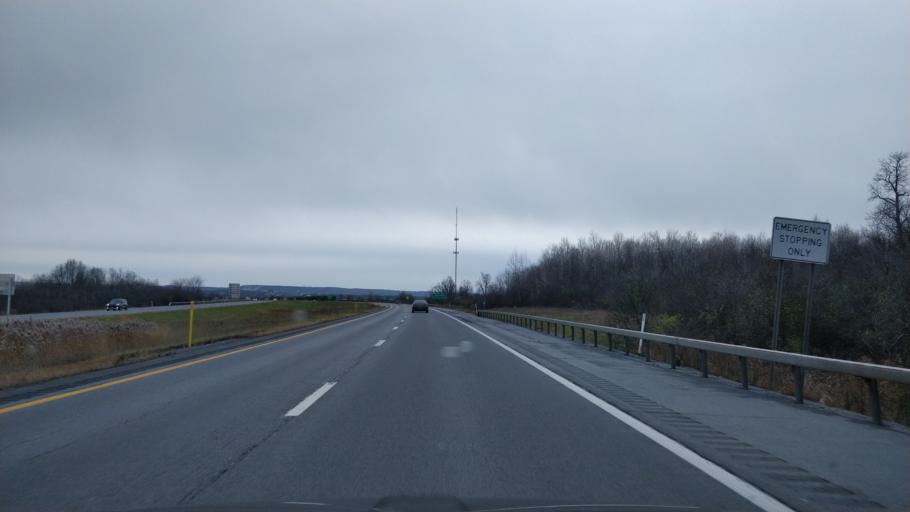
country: US
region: New York
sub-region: Jefferson County
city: Watertown
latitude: 44.0281
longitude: -75.9168
